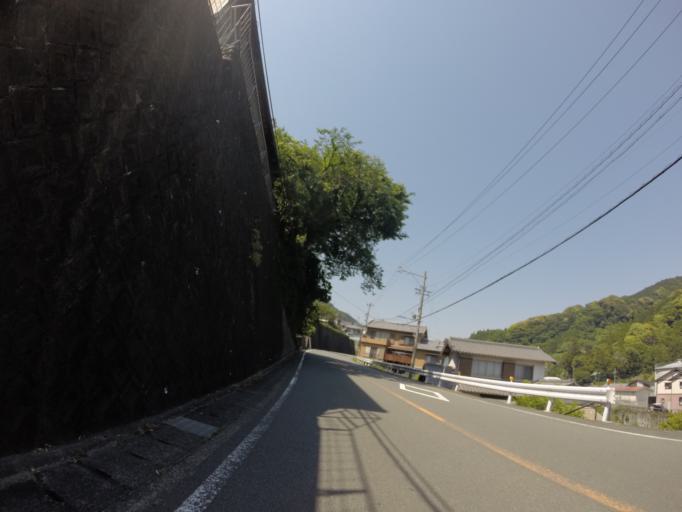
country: JP
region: Shizuoka
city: Fujinomiya
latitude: 35.1318
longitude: 138.5570
